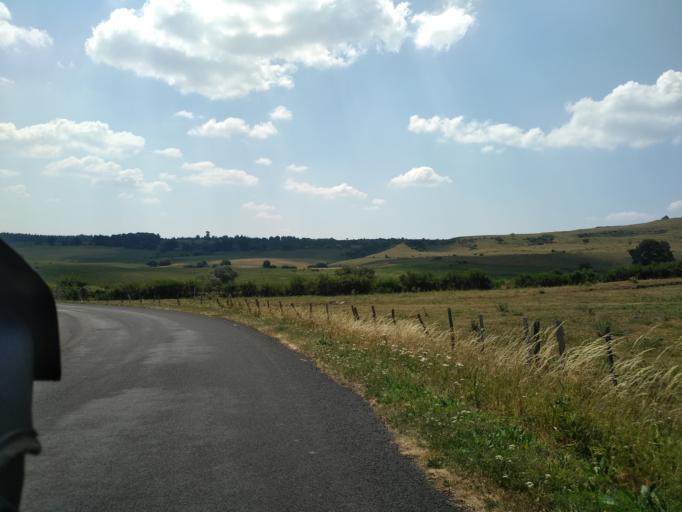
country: FR
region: Auvergne
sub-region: Departement du Puy-de-Dome
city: Mont-Dore
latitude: 45.5489
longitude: 2.8860
